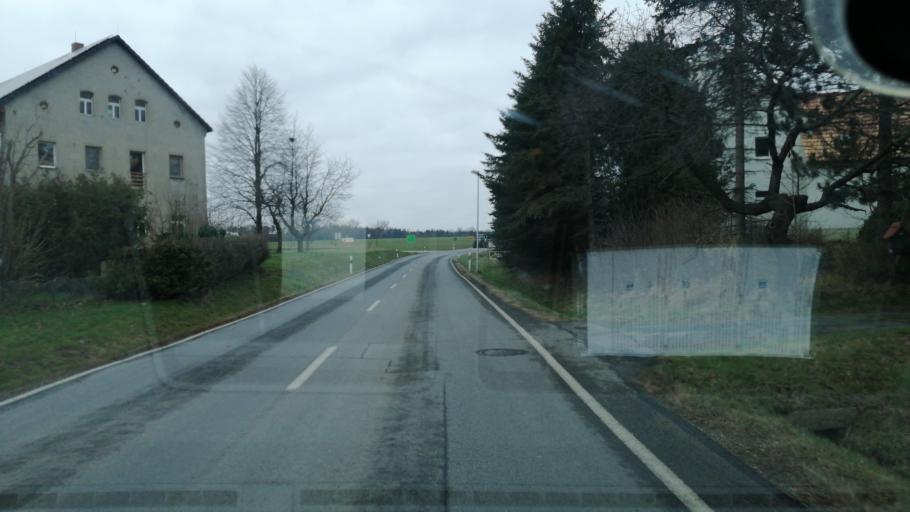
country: DE
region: Saxony
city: Sohland am Rotstein
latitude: 51.0706
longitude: 14.7778
